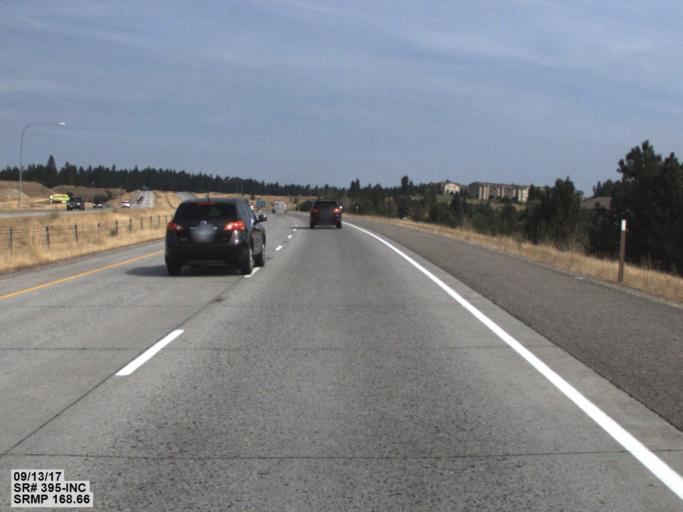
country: US
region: Washington
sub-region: Spokane County
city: Fairwood
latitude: 47.7979
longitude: -117.4063
